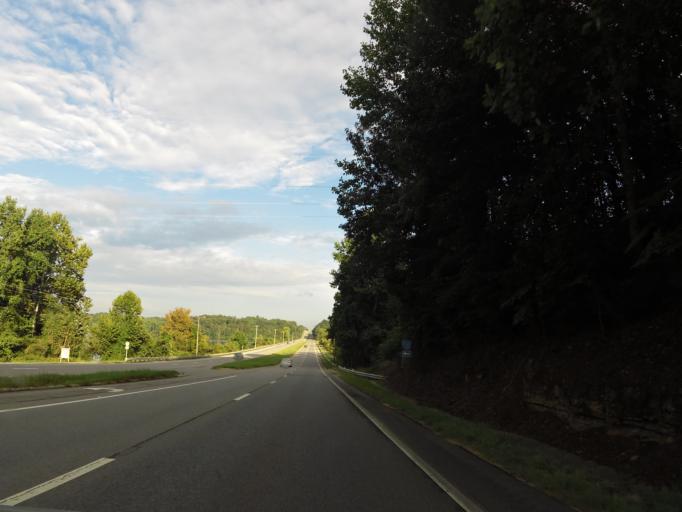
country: US
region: Alabama
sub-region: Lauderdale County
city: Rogersville
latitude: 34.8455
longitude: -87.3791
